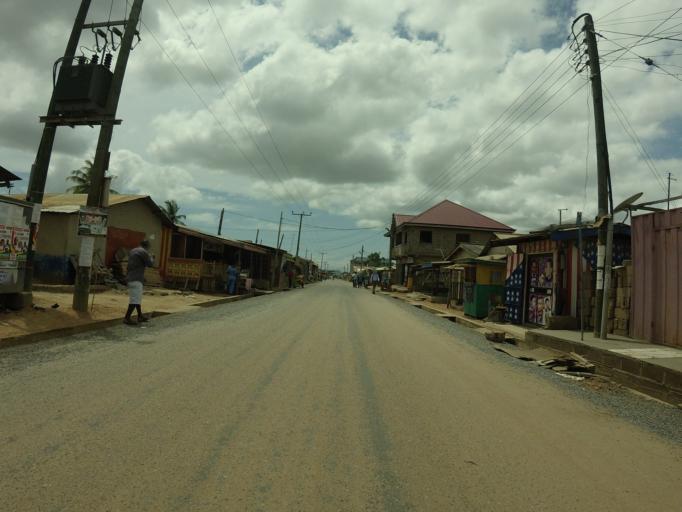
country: GH
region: Central
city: Kasoa
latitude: 5.5416
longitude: -0.3984
